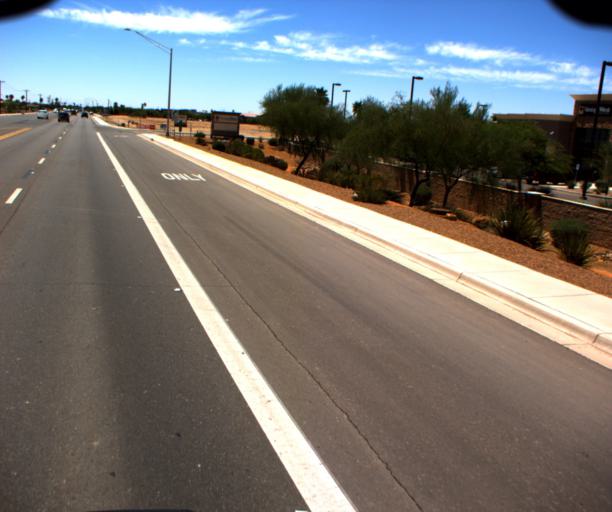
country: US
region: Arizona
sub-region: Pinal County
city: Casa Grande
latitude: 32.8797
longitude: -111.7002
